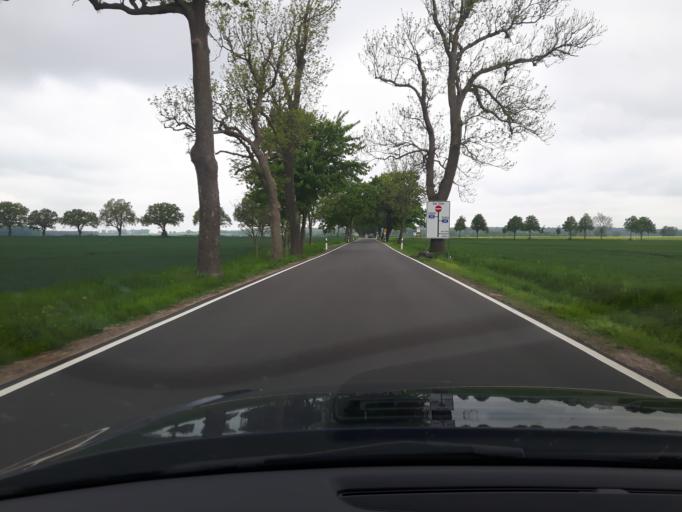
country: DE
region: Mecklenburg-Vorpommern
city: Bad Sulze
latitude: 54.0501
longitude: 12.6738
